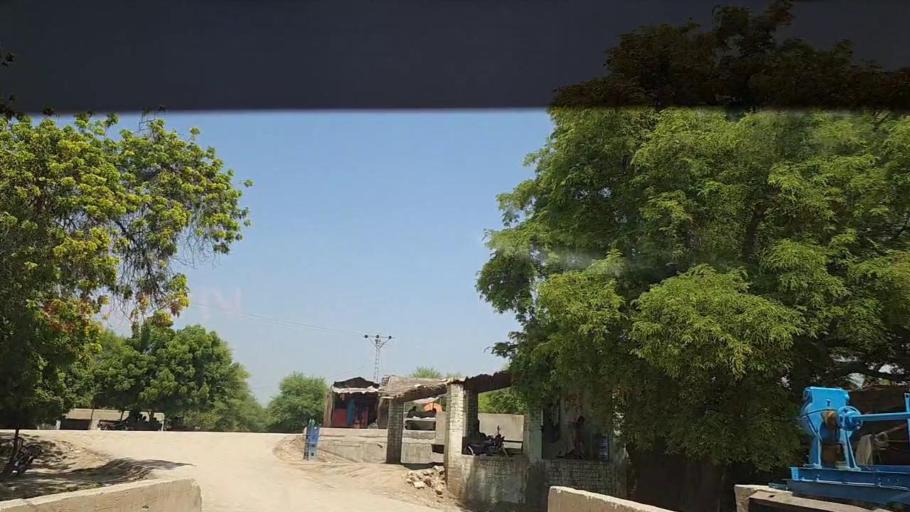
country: PK
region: Sindh
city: Ghauspur
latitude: 28.1643
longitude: 69.1371
